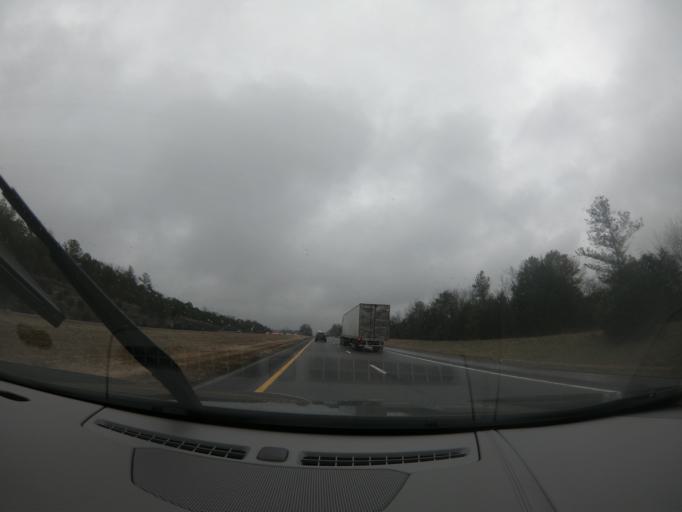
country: US
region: Tennessee
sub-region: Rutherford County
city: Plainview
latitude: 35.6939
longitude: -86.2990
